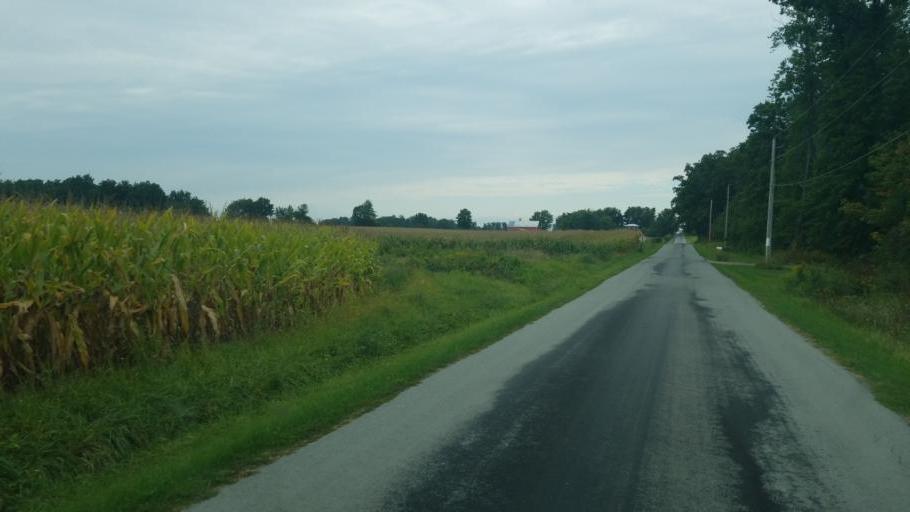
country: US
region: Ohio
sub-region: Wyandot County
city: Upper Sandusky
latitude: 40.8271
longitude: -83.1888
